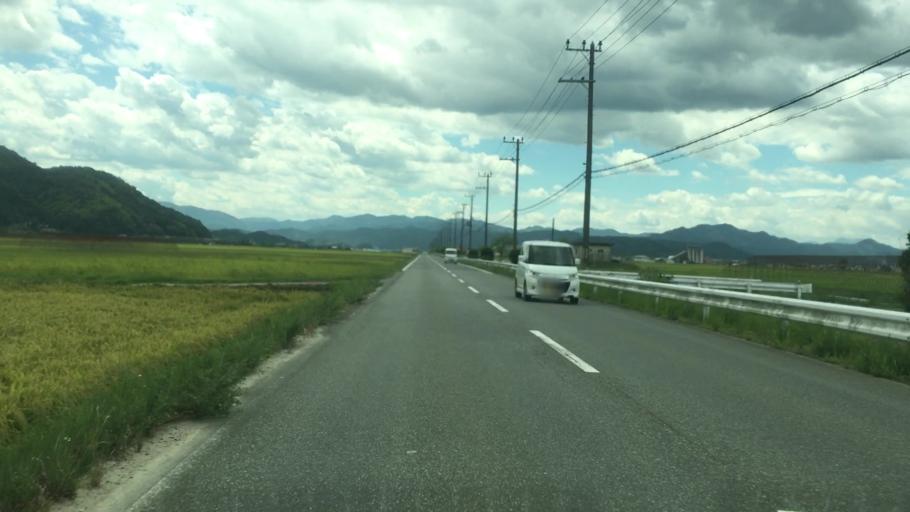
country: JP
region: Hyogo
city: Toyooka
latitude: 35.5384
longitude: 134.8397
